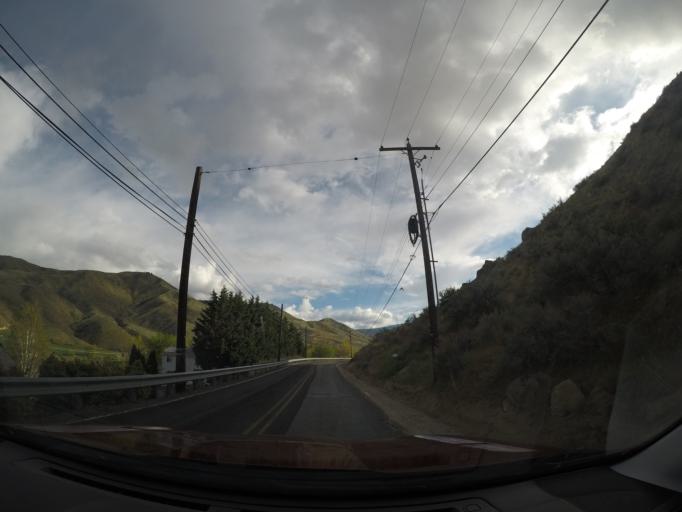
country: US
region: Washington
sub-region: Chelan County
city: South Wenatchee
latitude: 47.3863
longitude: -120.3110
